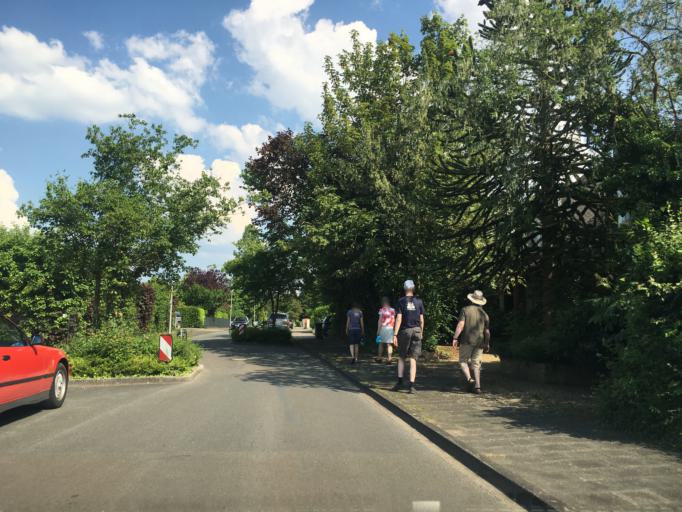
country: DE
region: North Rhine-Westphalia
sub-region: Regierungsbezirk Munster
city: Muenster
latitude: 51.9700
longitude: 7.5668
